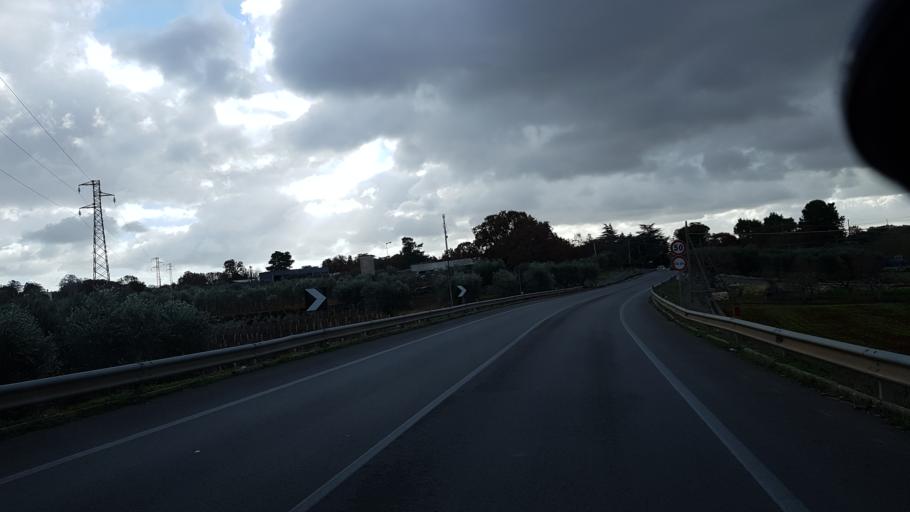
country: IT
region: Apulia
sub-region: Provincia di Bari
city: Locorotondo
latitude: 40.7808
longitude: 17.3387
